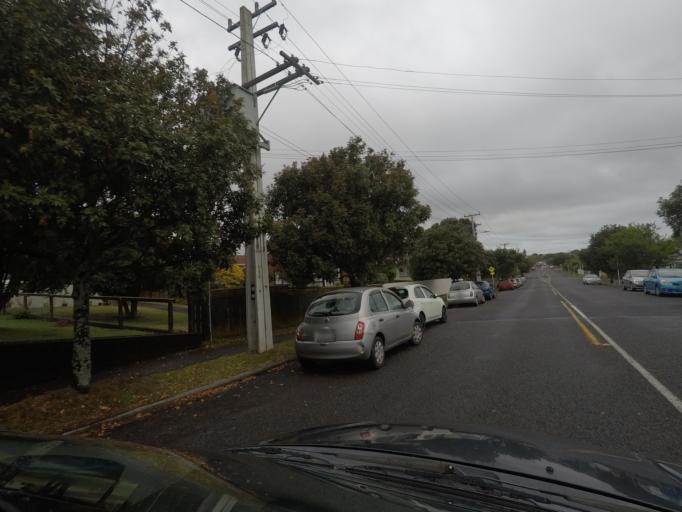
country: NZ
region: Auckland
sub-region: Auckland
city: Auckland
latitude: -36.8858
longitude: 174.7332
